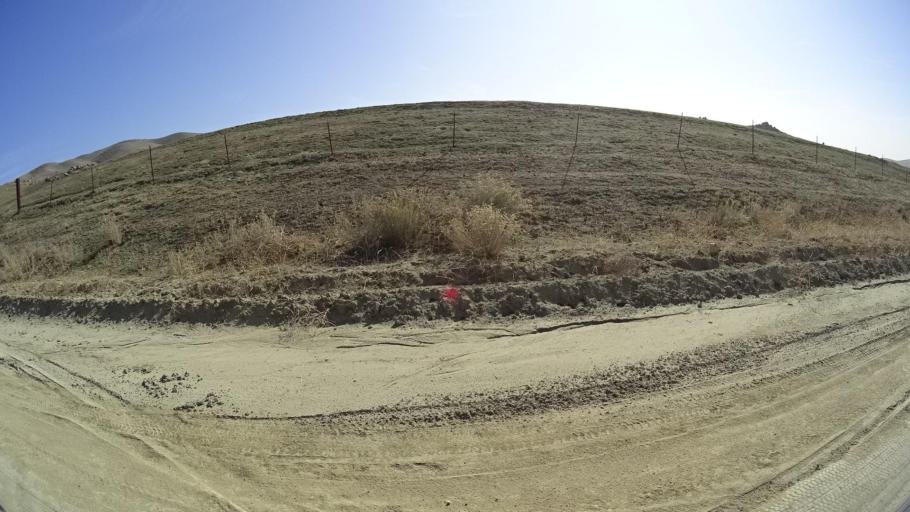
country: US
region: California
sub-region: Kern County
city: Oildale
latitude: 35.4748
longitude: -118.8265
